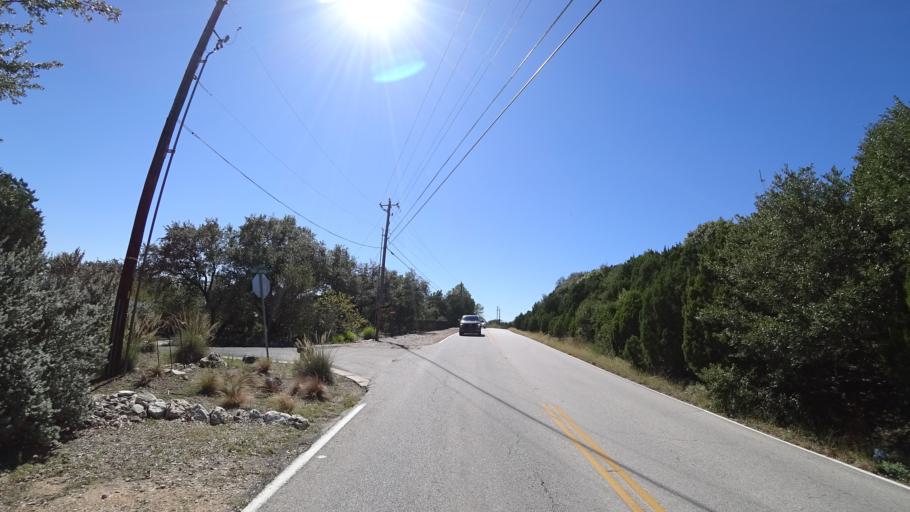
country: US
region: Texas
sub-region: Travis County
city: West Lake Hills
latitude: 30.3267
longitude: -97.7910
